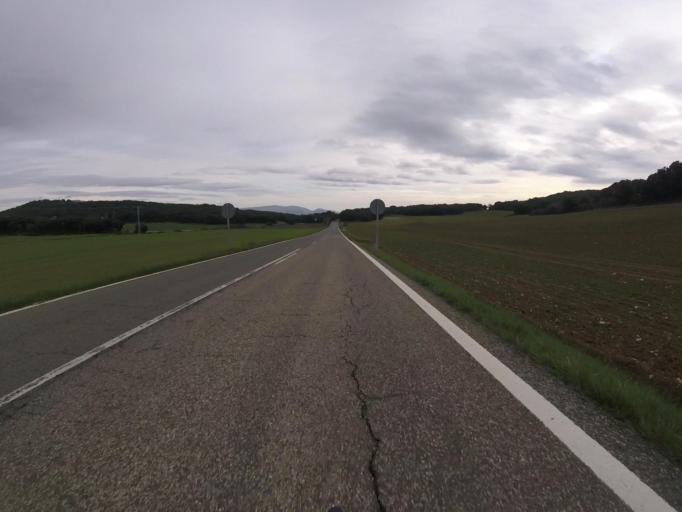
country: ES
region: Navarre
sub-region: Provincia de Navarra
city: Lezaun
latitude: 42.7400
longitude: -2.0203
